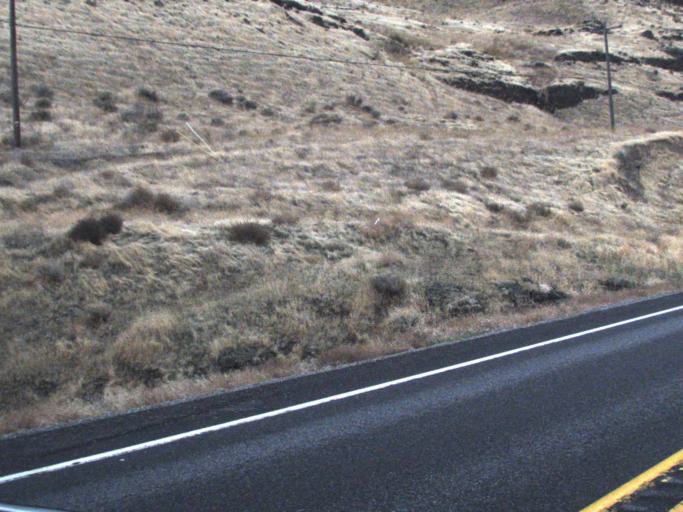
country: US
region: Washington
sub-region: Benton County
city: Finley
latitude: 46.0382
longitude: -118.9378
